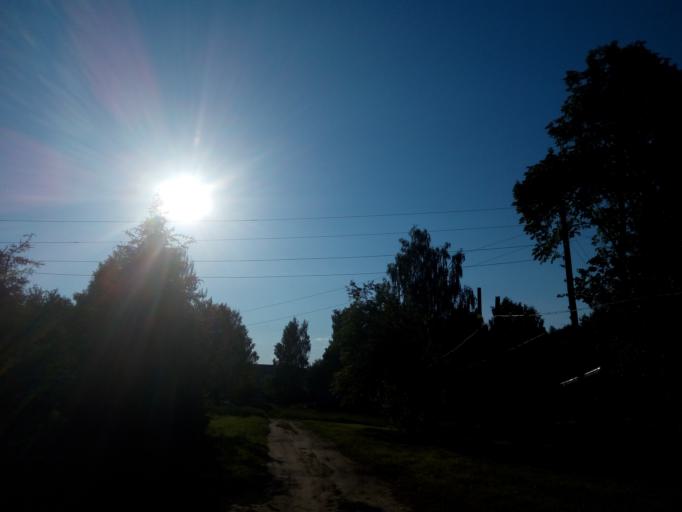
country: RU
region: Nizjnij Novgorod
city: Voskresenskoye
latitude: 56.7830
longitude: 45.5239
